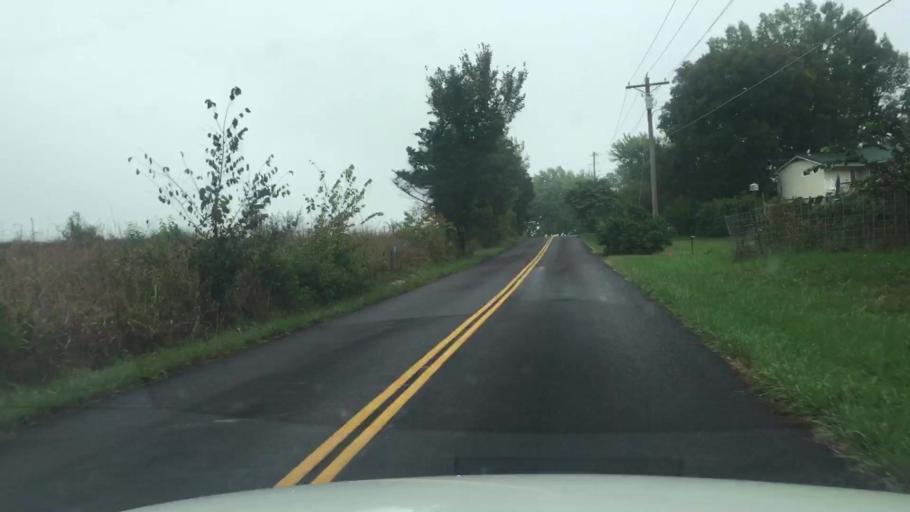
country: US
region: Missouri
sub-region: Boone County
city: Columbia
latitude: 38.8598
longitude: -92.3219
